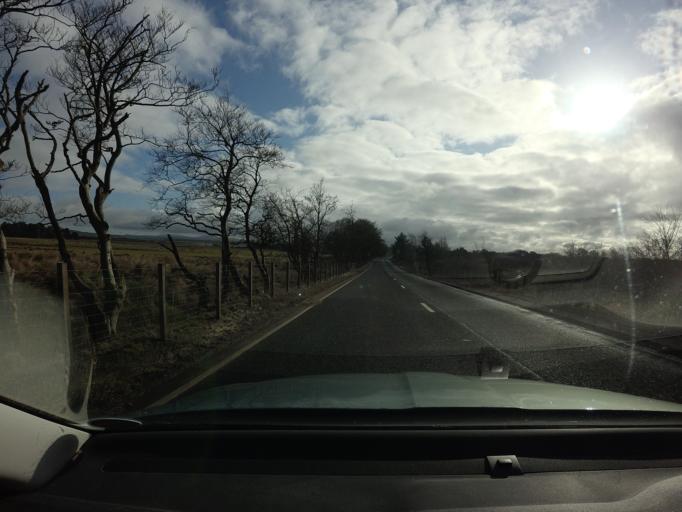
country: GB
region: Scotland
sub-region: South Lanarkshire
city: Forth
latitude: 55.7031
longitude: -3.7073
